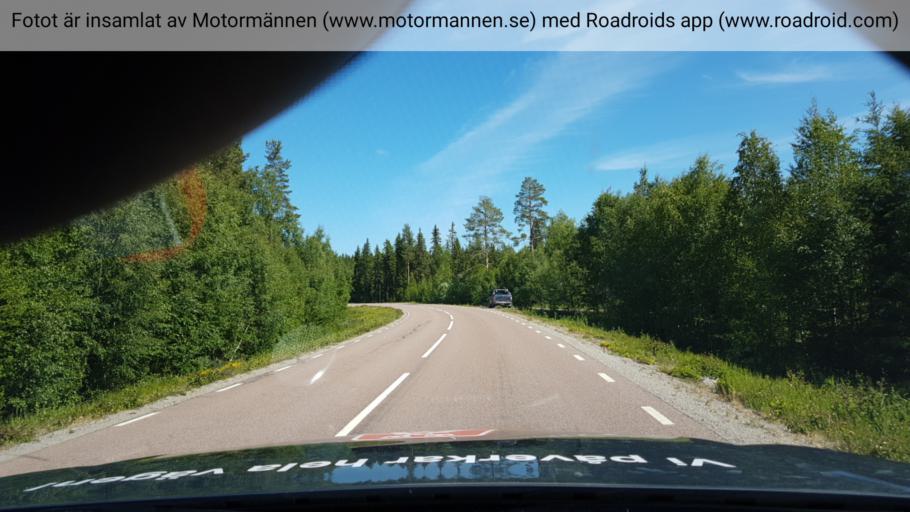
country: SE
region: Jaemtland
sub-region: Braecke Kommun
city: Braecke
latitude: 62.7506
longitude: 15.2689
